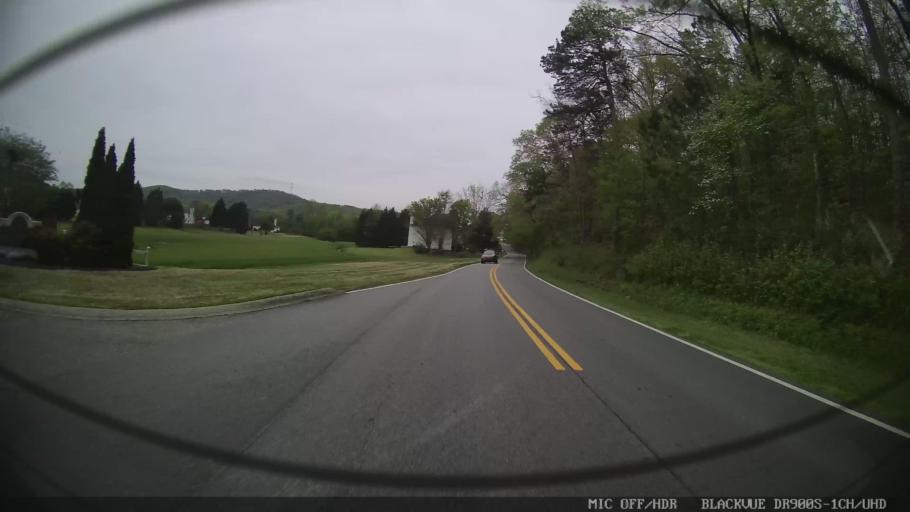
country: US
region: Georgia
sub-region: Bartow County
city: Cartersville
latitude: 34.2133
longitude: -84.7797
